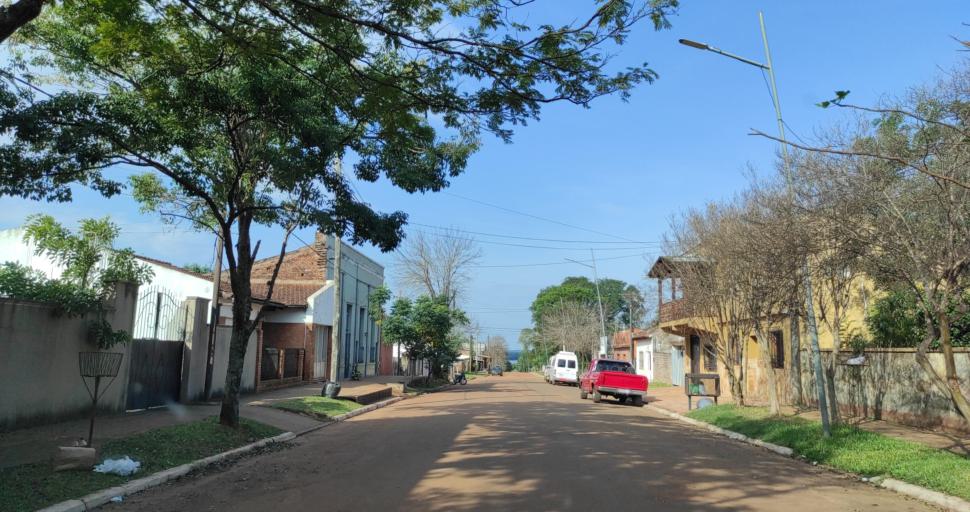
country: AR
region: Corrientes
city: Santo Tome
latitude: -28.5514
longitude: -56.0326
